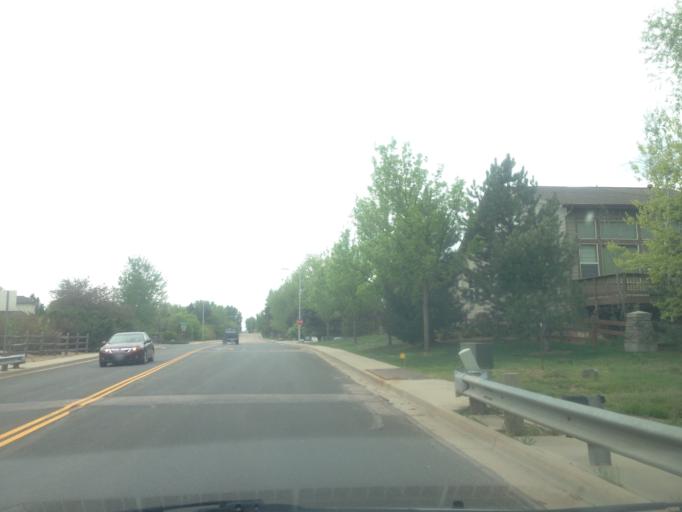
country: US
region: Colorado
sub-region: Boulder County
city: Longmont
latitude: 40.1348
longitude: -105.1215
